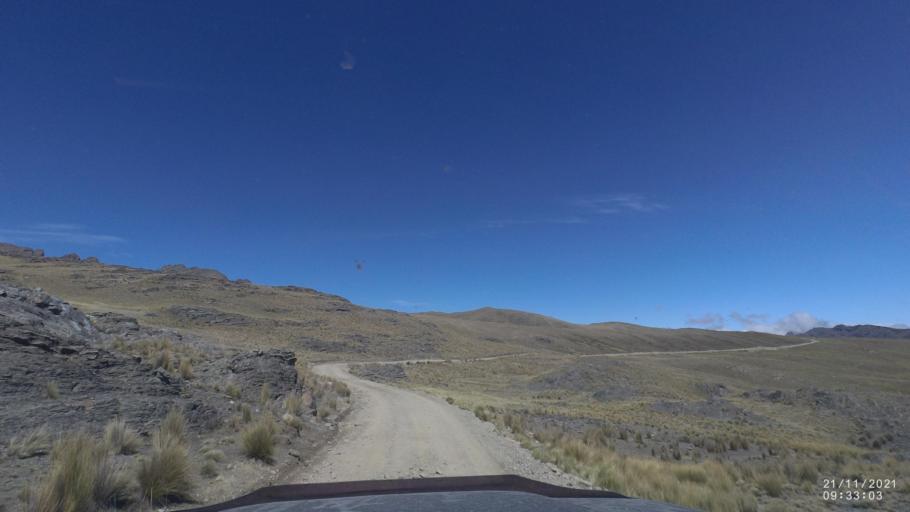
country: BO
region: Cochabamba
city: Cochabamba
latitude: -17.0631
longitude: -66.2564
